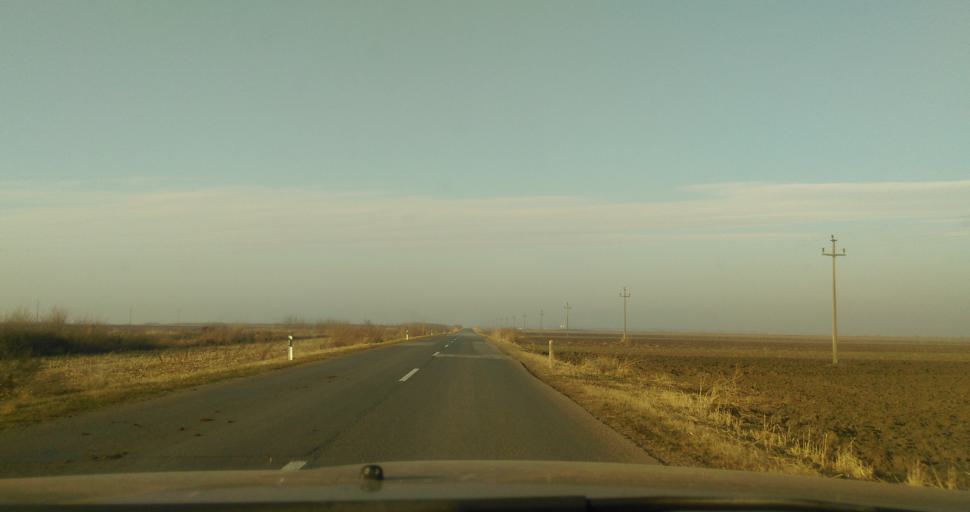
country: RS
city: Curug
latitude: 45.4869
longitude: 20.0379
